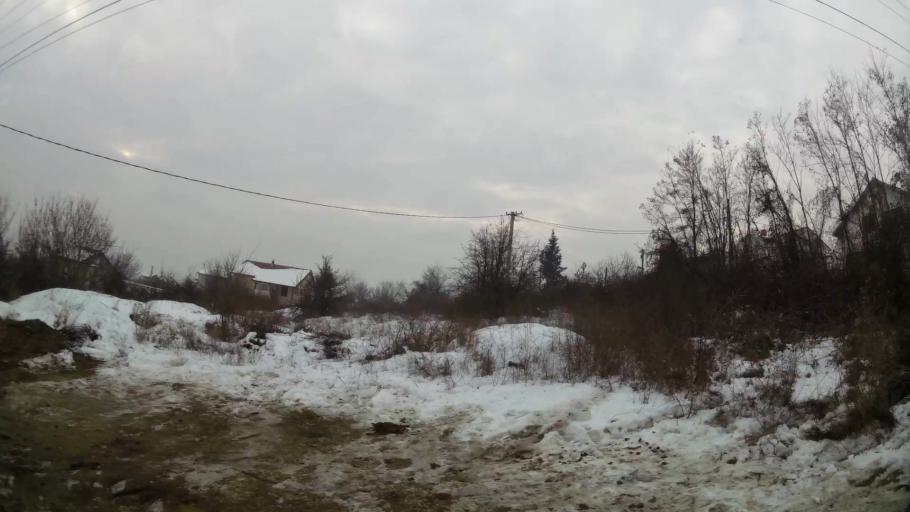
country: MK
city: Kondovo
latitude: 42.0458
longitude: 21.3413
